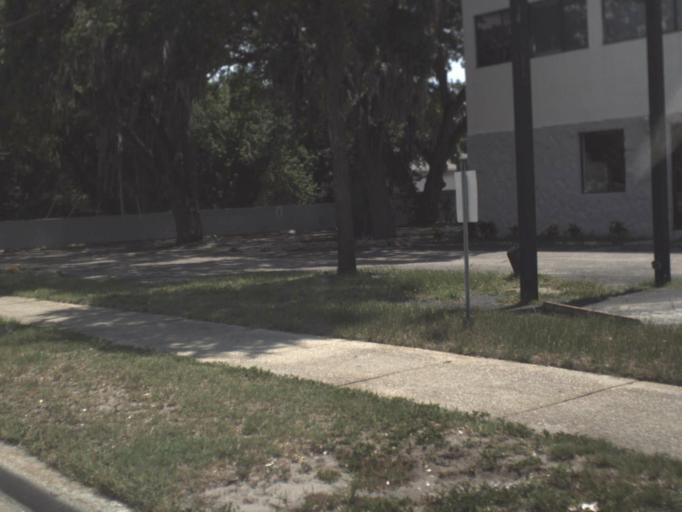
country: US
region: Florida
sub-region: Pinellas County
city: Saint Petersburg
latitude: 27.7518
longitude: -82.6795
